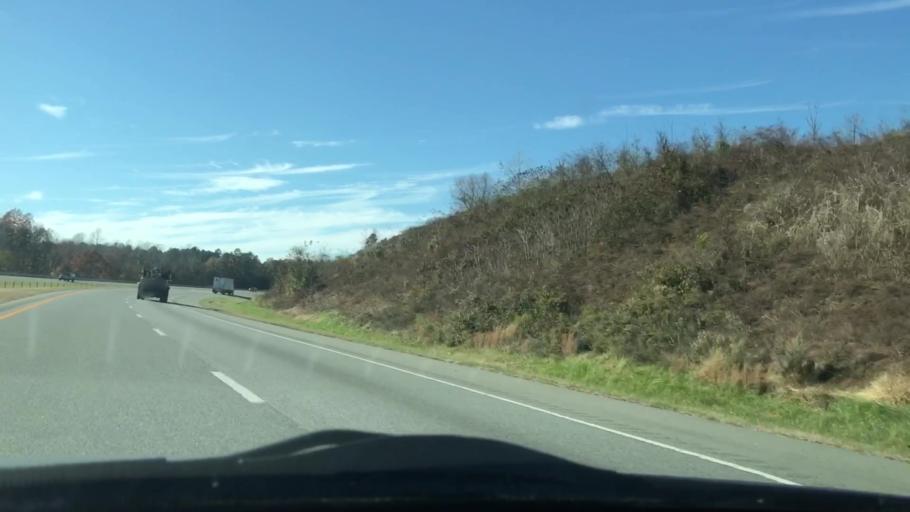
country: US
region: North Carolina
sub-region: Randolph County
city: Archdale
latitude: 35.9364
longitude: -79.9537
